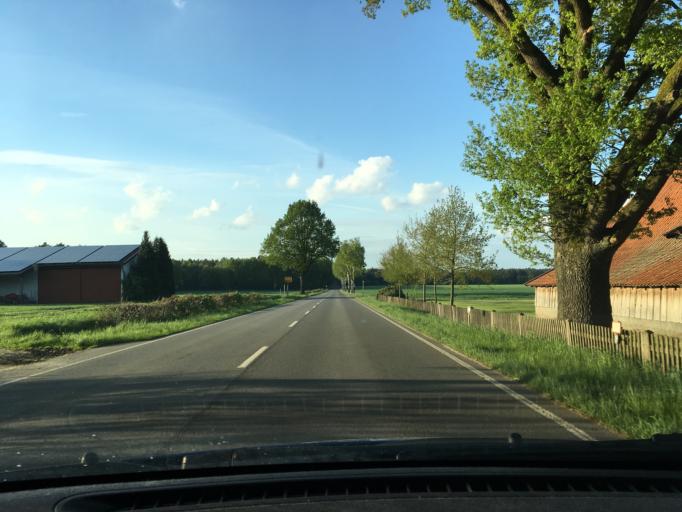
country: DE
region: Lower Saxony
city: Bergen
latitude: 52.8576
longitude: 9.9799
